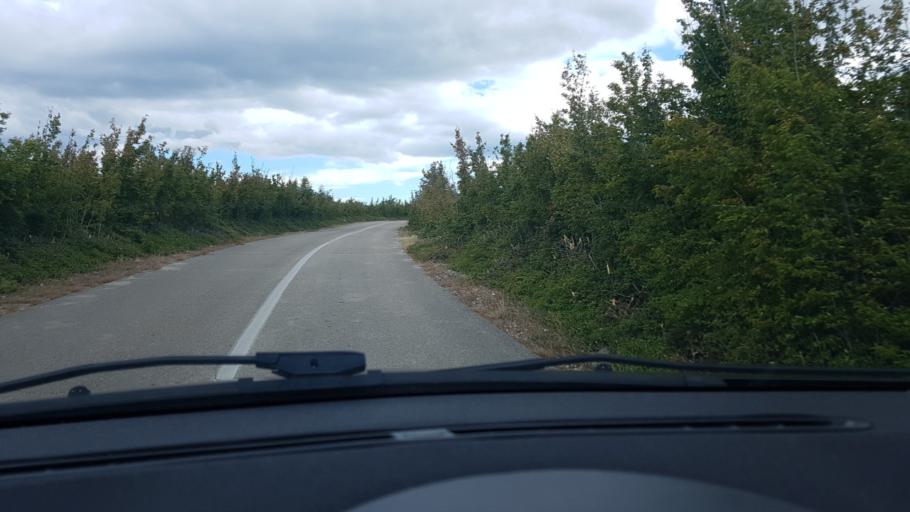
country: HR
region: Zadarska
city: Gracac
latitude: 44.1814
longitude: 15.8885
